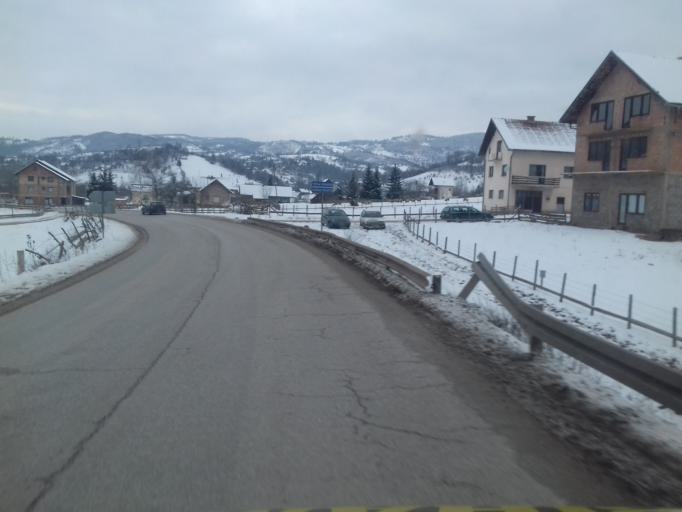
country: BA
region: Republika Srpska
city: Pale
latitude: 43.8722
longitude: 18.5883
